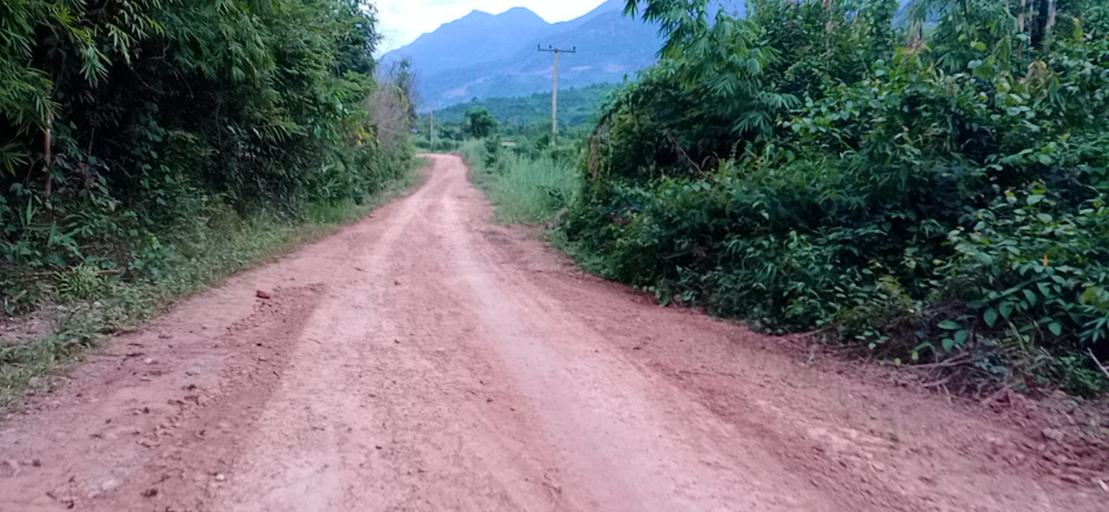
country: TH
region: Changwat Bueng Kan
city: Pak Khat
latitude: 18.5525
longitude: 103.1622
